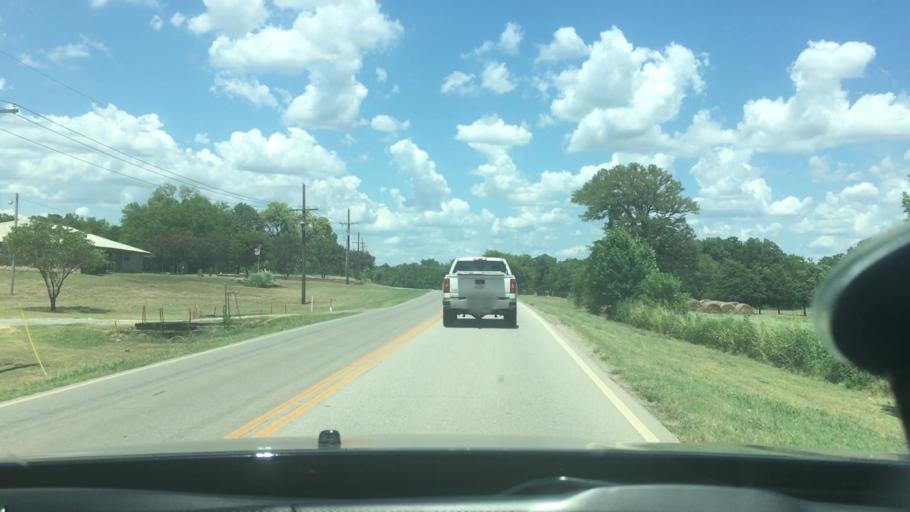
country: US
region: Oklahoma
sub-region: Bryan County
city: Durant
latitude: 33.9811
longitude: -96.3719
